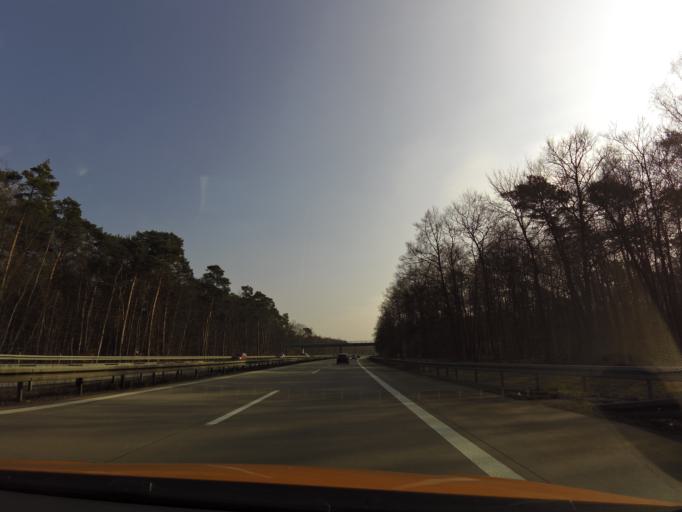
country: DE
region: Brandenburg
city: Berkenbruck
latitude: 52.3429
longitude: 14.1897
